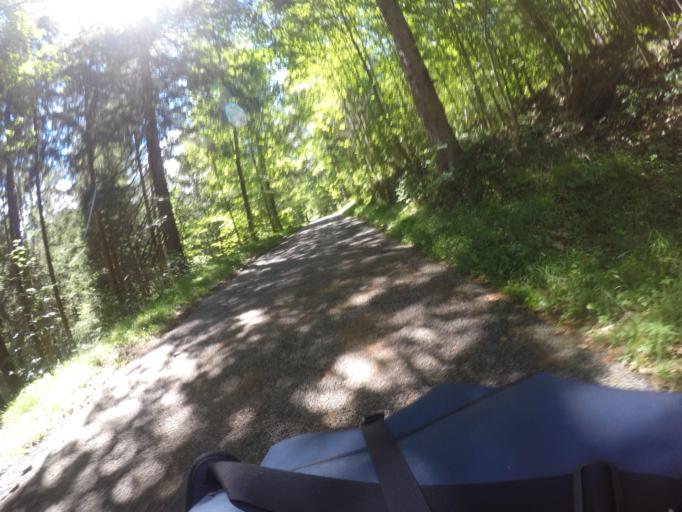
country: AT
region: Tyrol
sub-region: Politischer Bezirk Reutte
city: Musau
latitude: 47.5627
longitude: 10.6660
